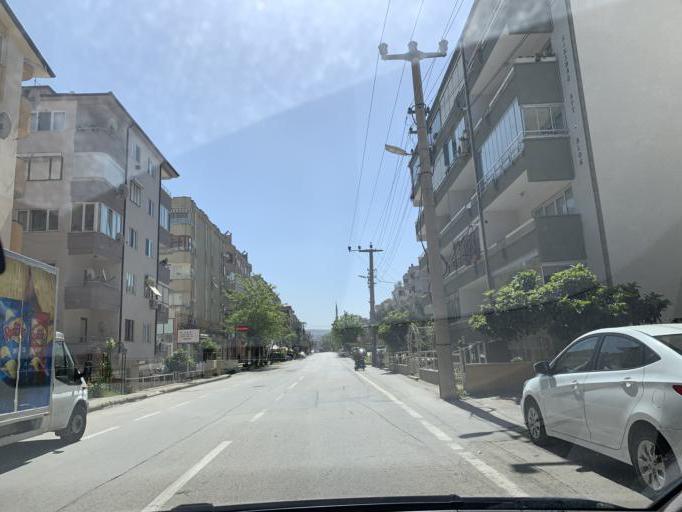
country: TR
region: Bursa
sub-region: Mudanya
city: Mudanya
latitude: 40.3606
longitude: 28.9113
